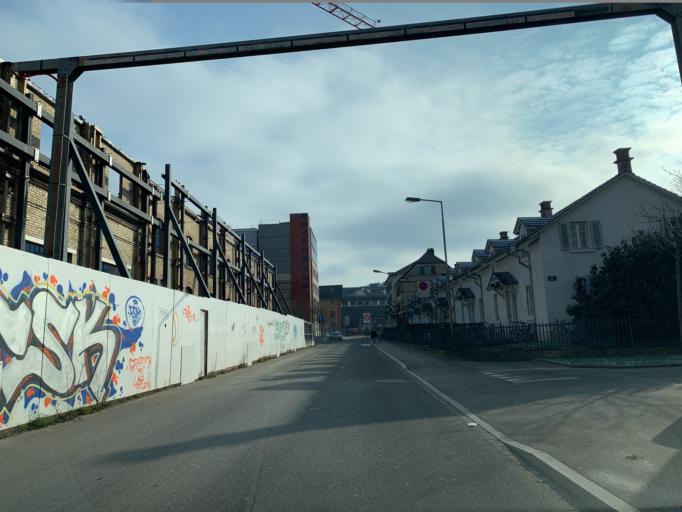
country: CH
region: Zurich
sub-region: Bezirk Winterthur
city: Stadt Winterthur (Kreis 1) / Toessfeld
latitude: 47.4949
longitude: 8.7150
